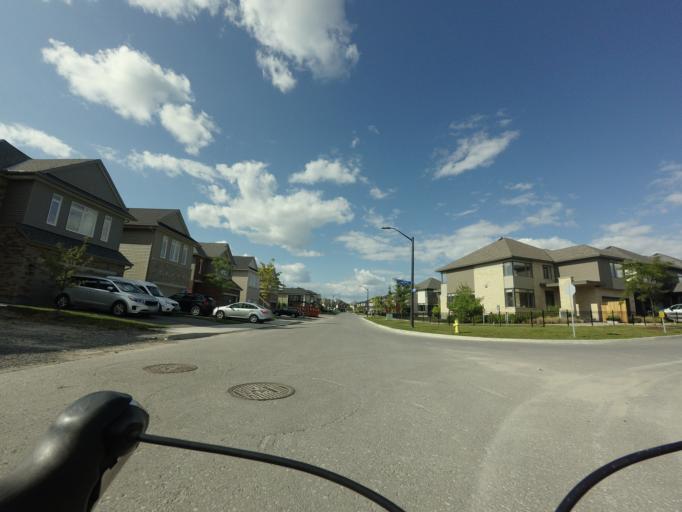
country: CA
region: Ontario
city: Bells Corners
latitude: 45.2843
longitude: -75.8451
